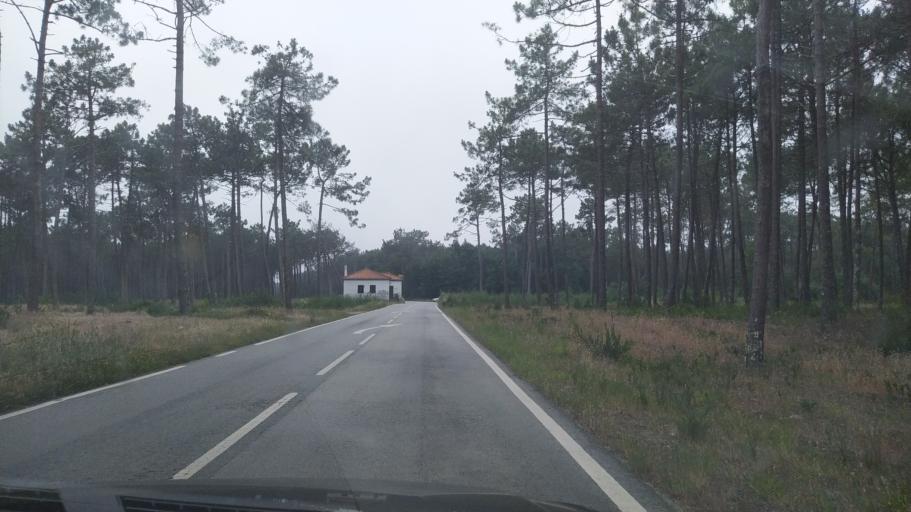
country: PT
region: Aveiro
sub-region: Ilhavo
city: Gafanha da Encarnacao
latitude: 40.5795
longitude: -8.7337
